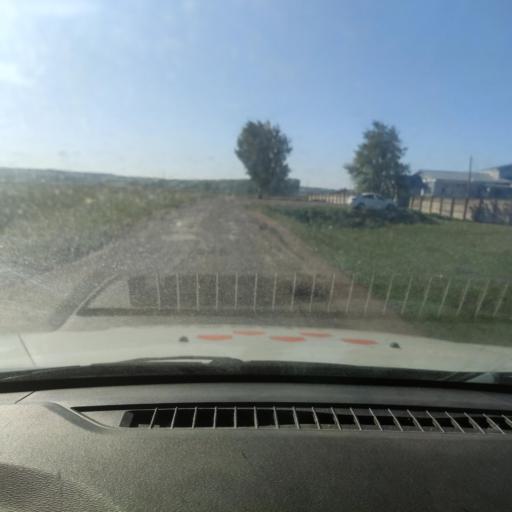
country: RU
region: Bashkortostan
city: Mikhaylovka
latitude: 54.9633
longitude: 55.7667
